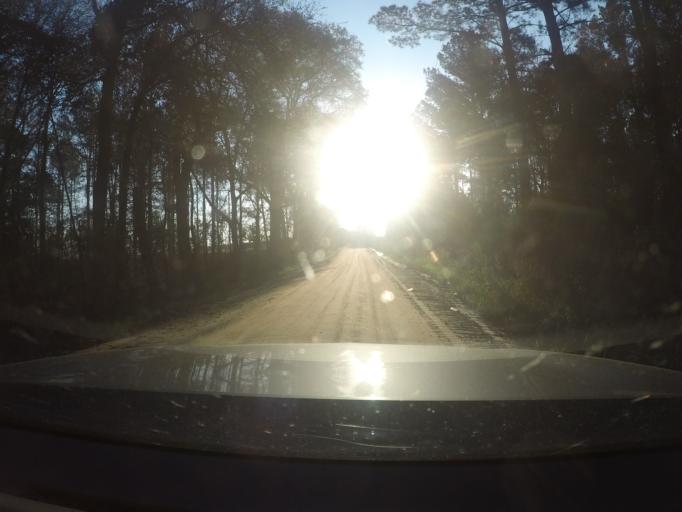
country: US
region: Georgia
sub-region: Bulloch County
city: Brooklet
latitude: 32.3011
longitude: -81.7268
